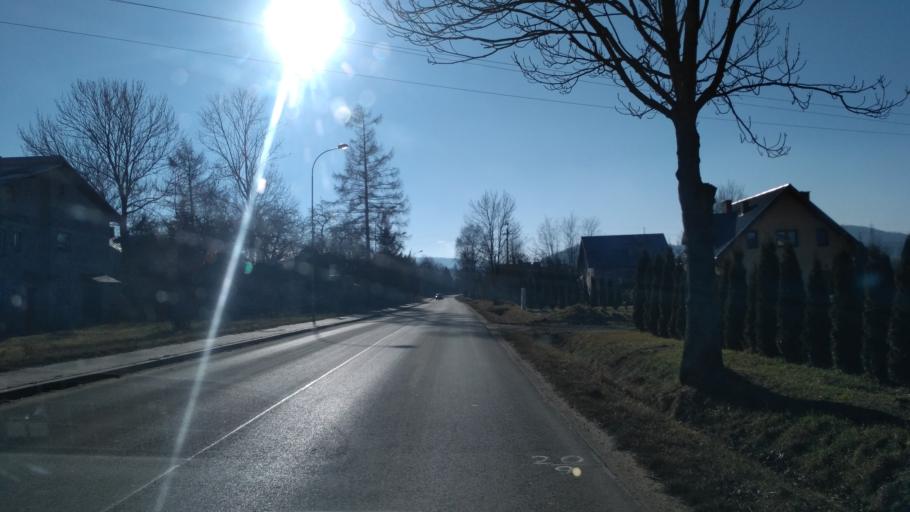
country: PL
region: Subcarpathian Voivodeship
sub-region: Powiat krosnienski
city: Rymanow
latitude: 49.5861
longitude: 21.8668
